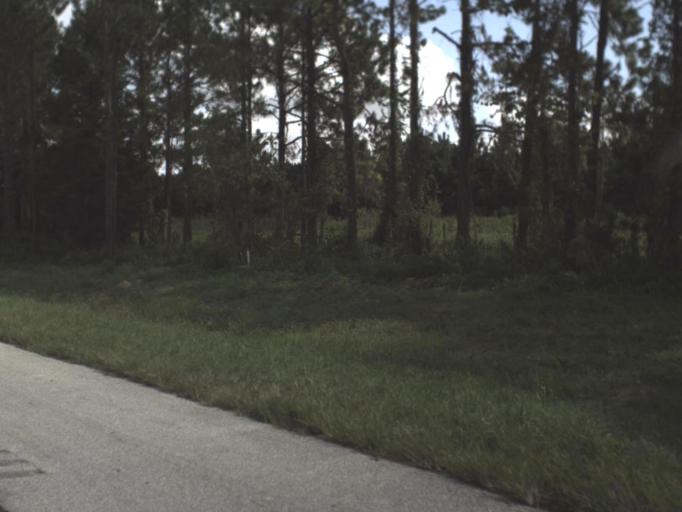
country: US
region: Florida
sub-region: Pasco County
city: Wesley Chapel
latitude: 28.2806
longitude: -82.3261
